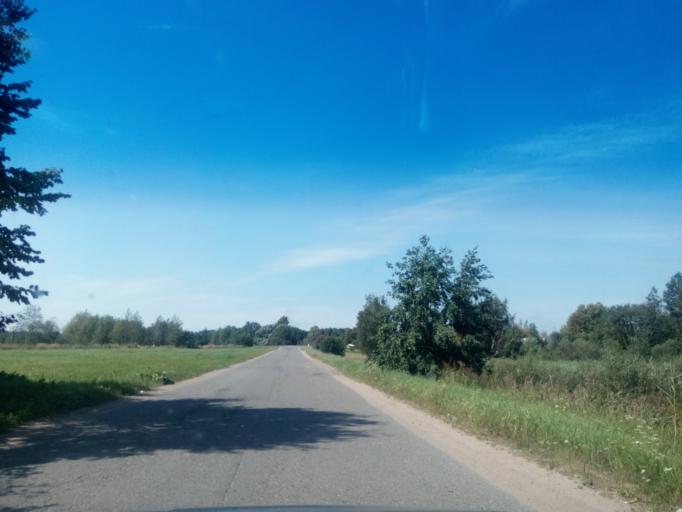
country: BY
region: Vitebsk
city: Vyerkhnyadzvinsk
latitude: 55.8362
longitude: 27.7341
